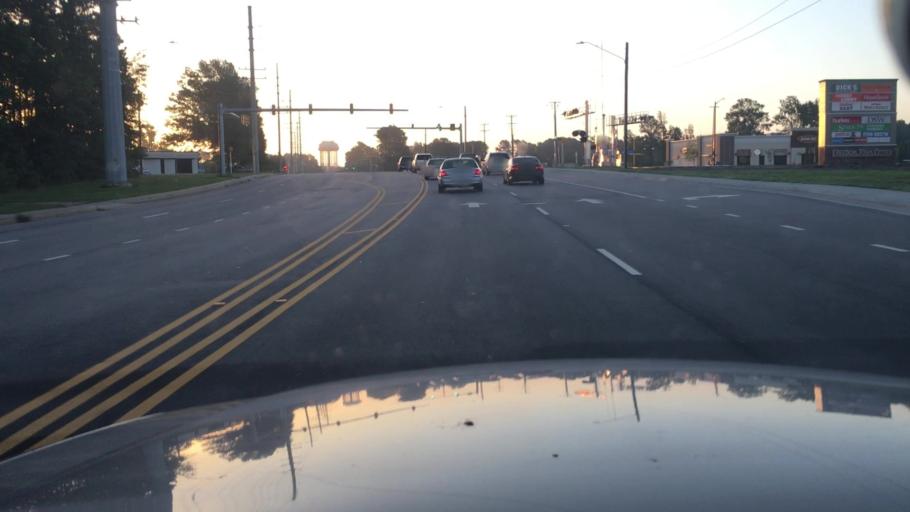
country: US
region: North Carolina
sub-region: Cumberland County
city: Fort Bragg
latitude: 35.0591
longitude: -78.9682
